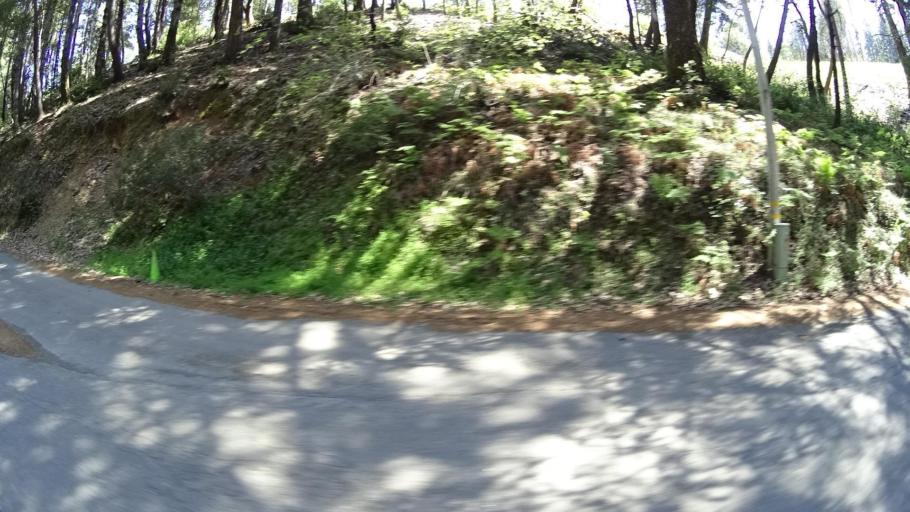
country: US
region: California
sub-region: Humboldt County
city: Redway
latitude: 40.1015
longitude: -123.9499
